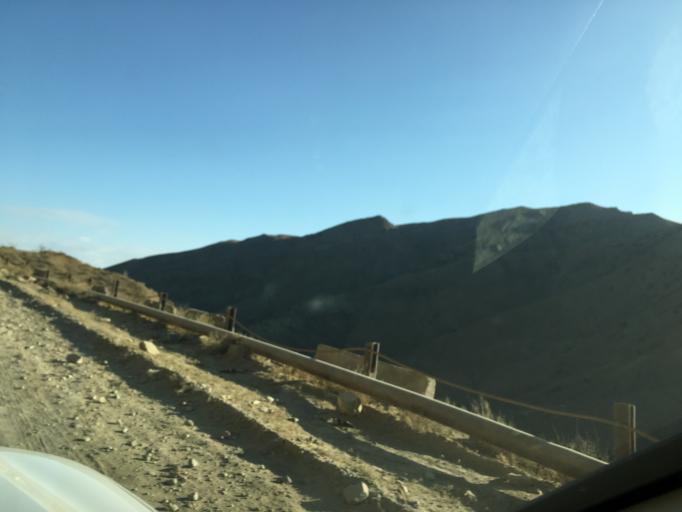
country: TM
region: Ahal
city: Baharly
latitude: 38.4439
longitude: 57.0459
